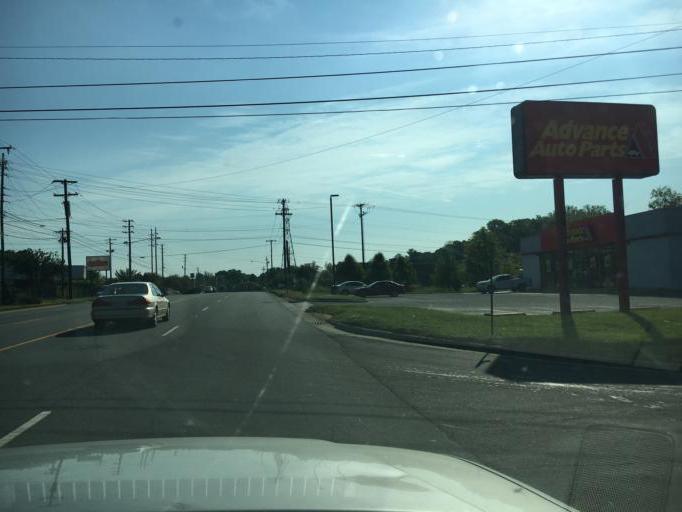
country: US
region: North Carolina
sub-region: Burke County
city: Morganton
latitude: 35.7344
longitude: -81.6846
